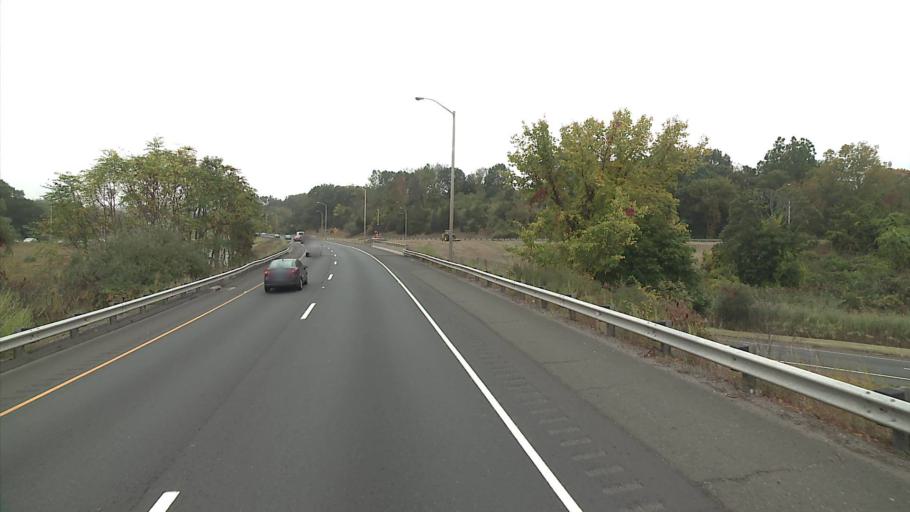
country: US
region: Connecticut
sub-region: Fairfield County
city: Danbury
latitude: 41.4185
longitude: -73.4237
